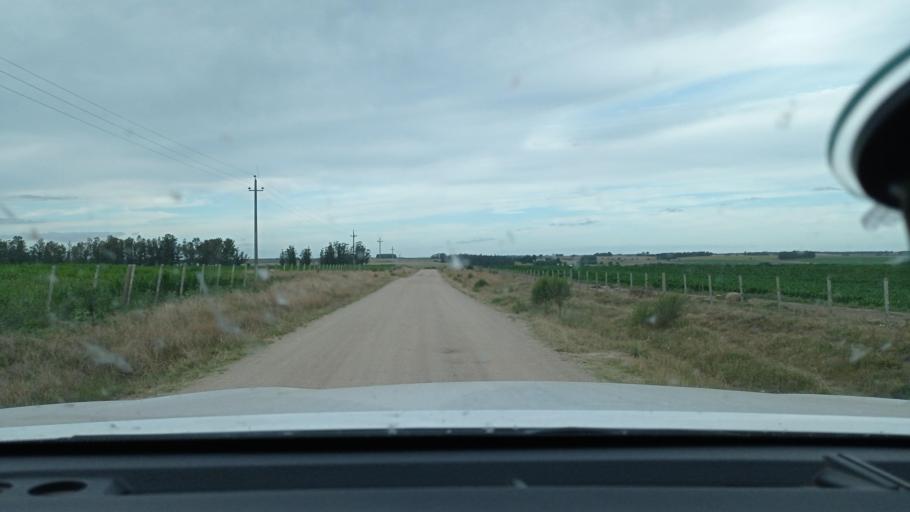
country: UY
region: Florida
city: Casupa
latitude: -34.1031
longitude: -55.7531
